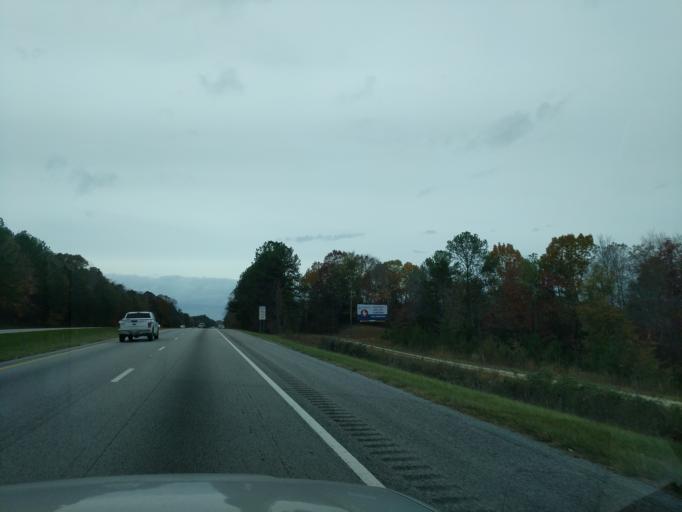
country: US
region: South Carolina
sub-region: Laurens County
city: Joanna
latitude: 34.4442
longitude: -81.7693
